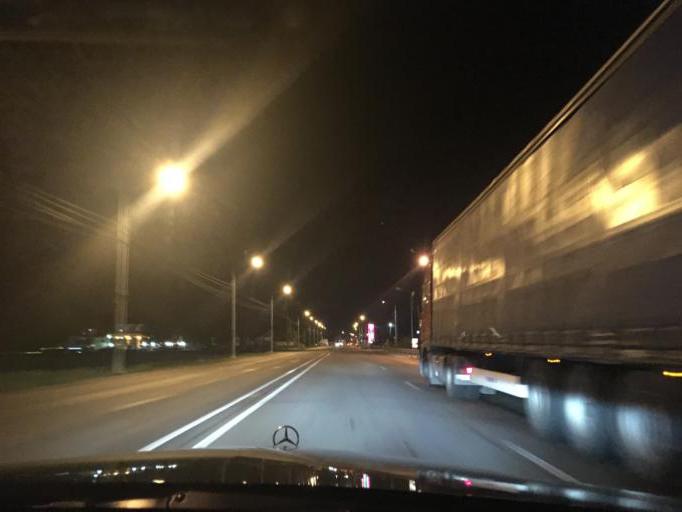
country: RO
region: Bihor
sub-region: Comuna Bors
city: Bors
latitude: 47.1095
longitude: 21.8191
